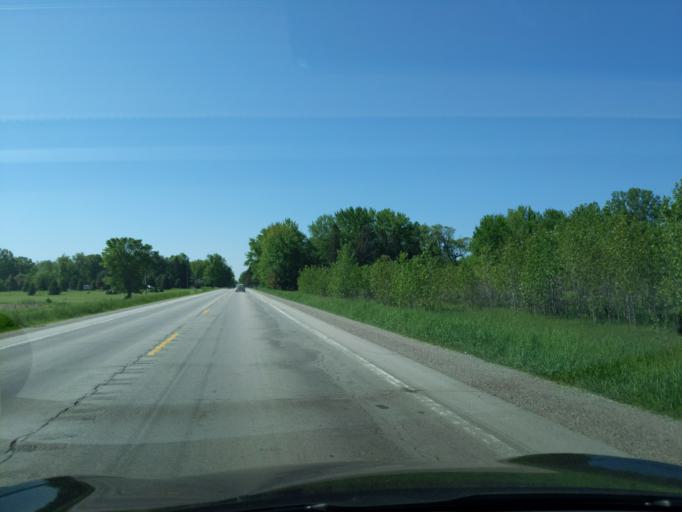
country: US
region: Michigan
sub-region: Ingham County
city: Stockbridge
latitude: 42.4892
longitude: -84.1901
